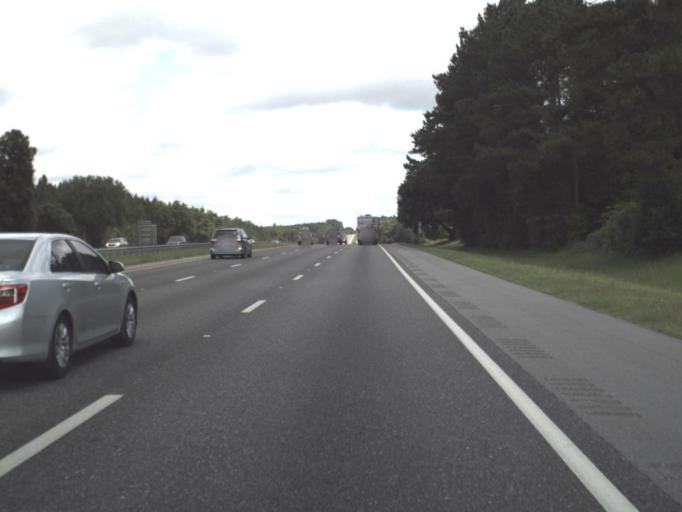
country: US
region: Florida
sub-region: Columbia County
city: Watertown
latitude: 30.0130
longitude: -82.6066
